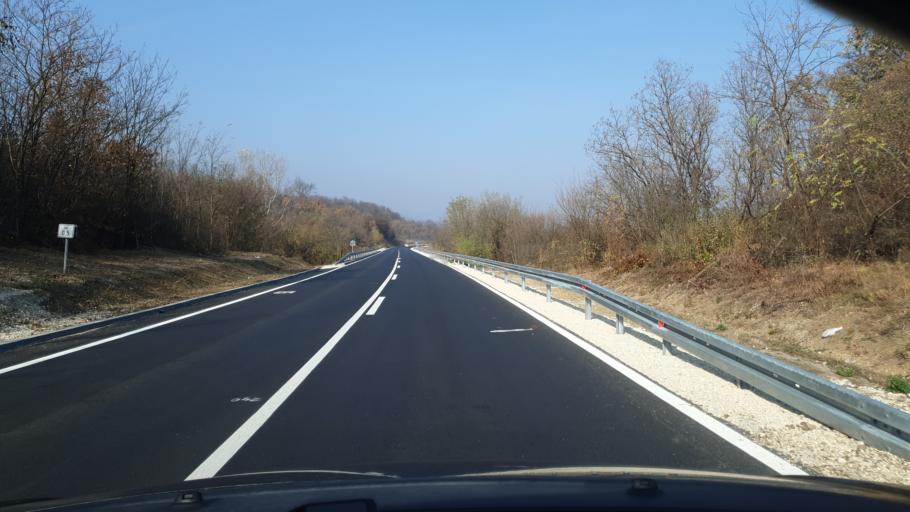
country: RS
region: Central Serbia
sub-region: Zajecarski Okrug
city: Zajecar
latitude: 43.9633
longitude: 22.2981
